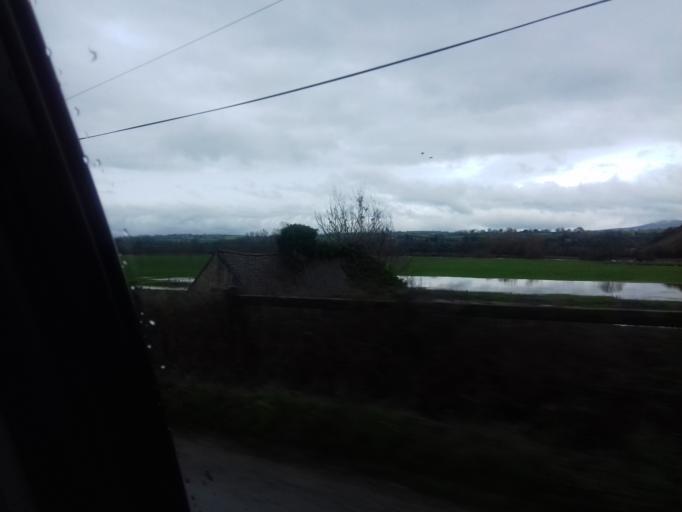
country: IE
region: Leinster
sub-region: County Carlow
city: Bagenalstown
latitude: 52.6403
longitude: -6.9927
